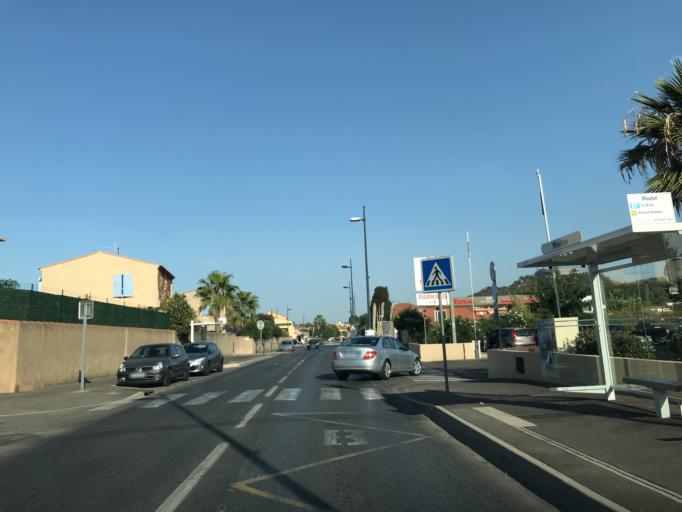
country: FR
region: Provence-Alpes-Cote d'Azur
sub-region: Departement du Var
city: Six-Fours-les-Plages
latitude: 43.0883
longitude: 5.8532
